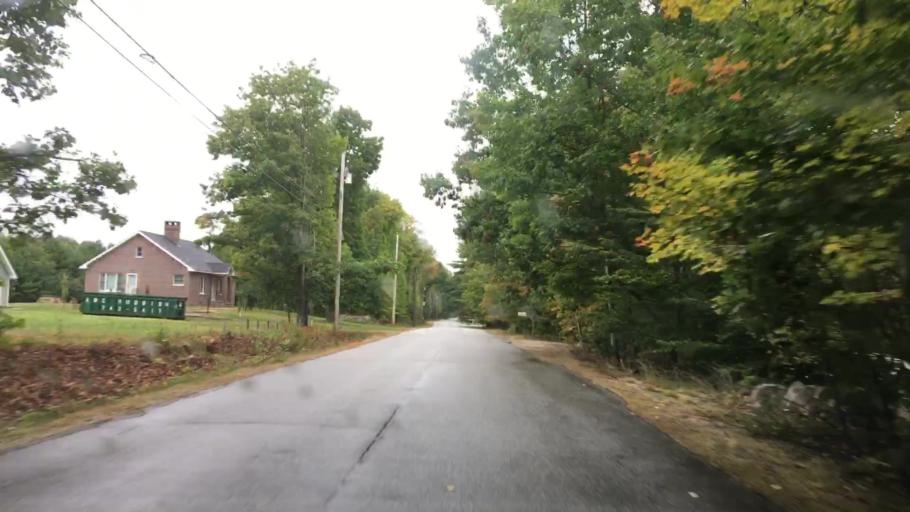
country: US
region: Maine
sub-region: Cumberland County
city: Harrison
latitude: 44.0639
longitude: -70.6276
